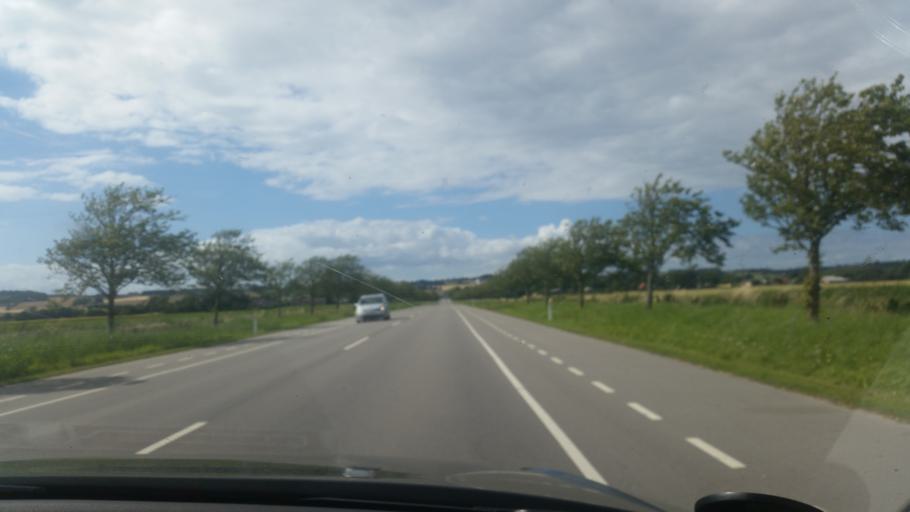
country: DK
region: Zealand
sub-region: Odsherred Kommune
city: Horve
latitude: 55.7950
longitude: 11.4532
